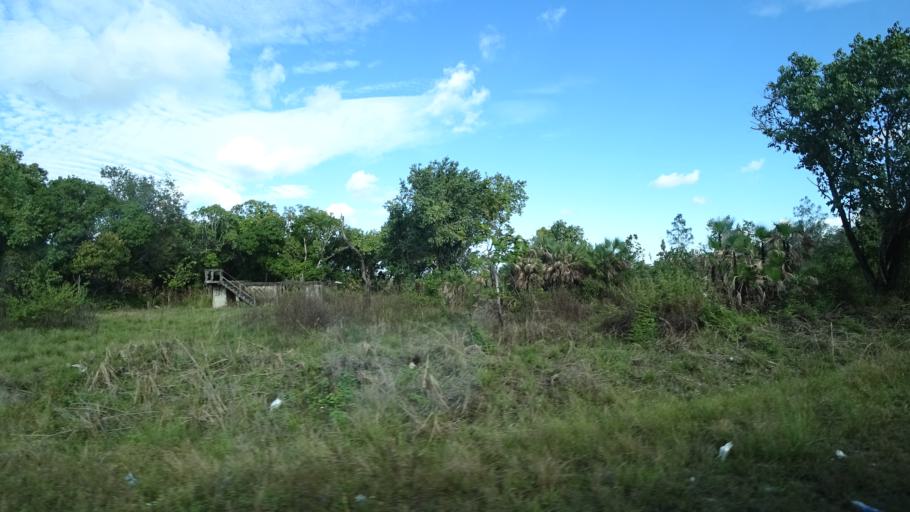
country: BZ
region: Belize
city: Belize City
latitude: 17.5628
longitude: -88.4056
